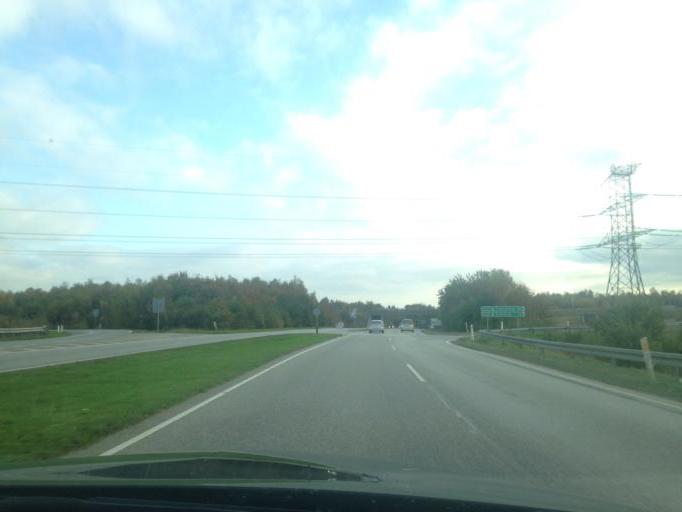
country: DK
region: South Denmark
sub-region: Kolding Kommune
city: Kolding
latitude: 55.5346
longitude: 9.4928
